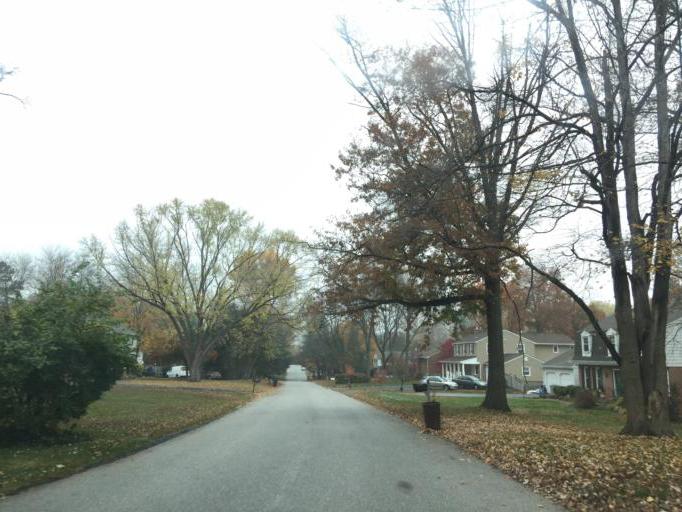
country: US
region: Maryland
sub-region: Howard County
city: Riverside
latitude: 39.1969
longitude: -76.8581
